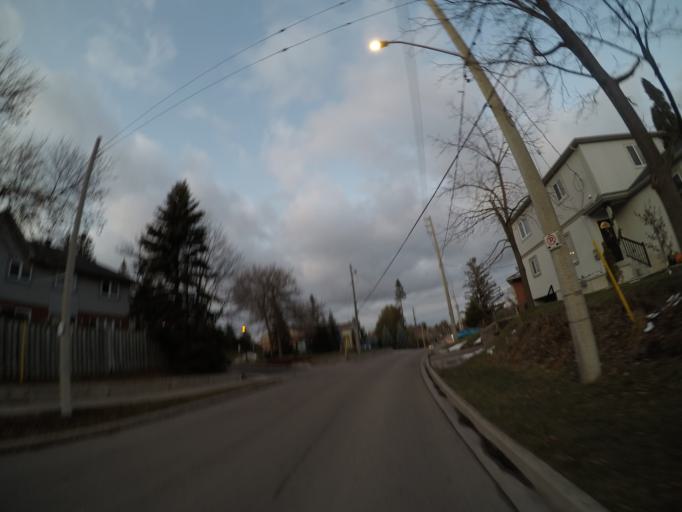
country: CA
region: Ontario
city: Waterloo
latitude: 43.4854
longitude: -80.4842
